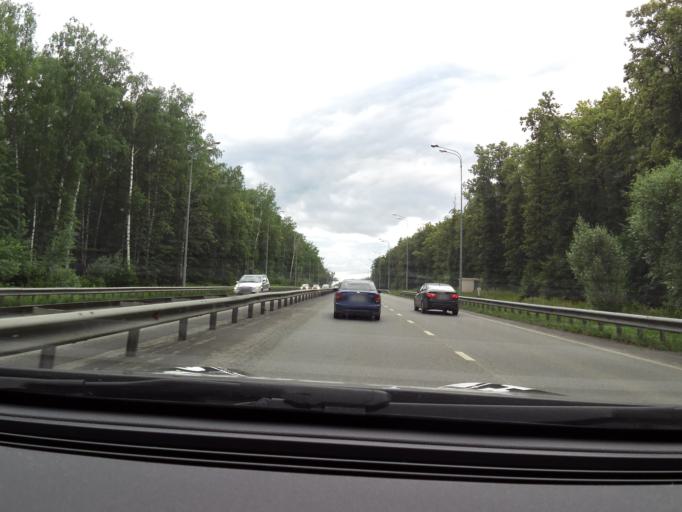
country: RU
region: Tatarstan
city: Staroye Arakchino
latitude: 55.8441
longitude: 48.9346
